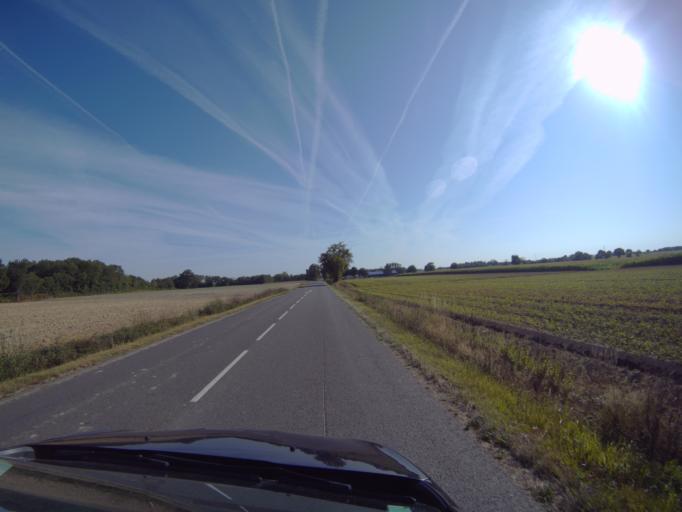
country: FR
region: Pays de la Loire
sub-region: Departement de la Vendee
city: Nieul-le-Dolent
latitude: 46.5273
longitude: -1.5496
